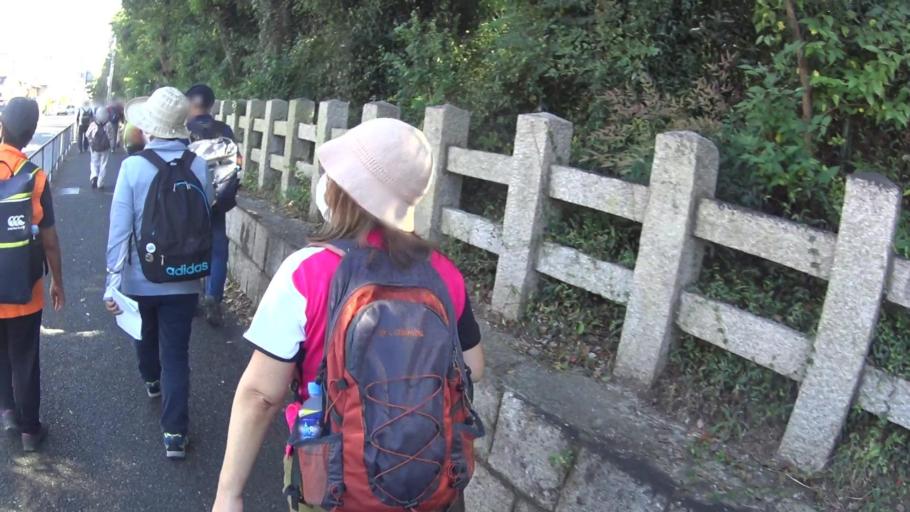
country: JP
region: Mie
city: Ise
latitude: 34.5341
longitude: 136.5753
